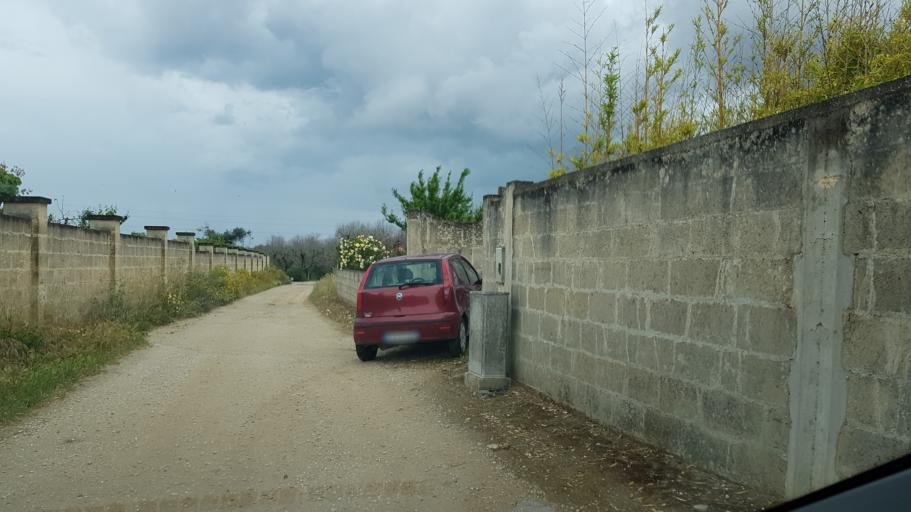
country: IT
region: Apulia
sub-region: Provincia di Brindisi
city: Torchiarolo
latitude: 40.4919
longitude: 18.0489
